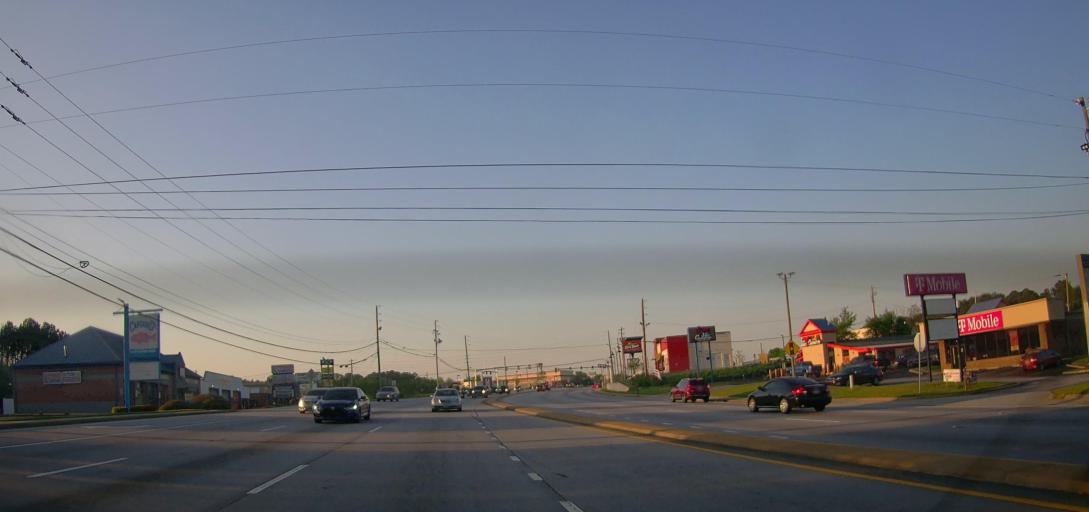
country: US
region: Georgia
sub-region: Rockdale County
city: Conyers
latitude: 33.6439
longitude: -84.0145
